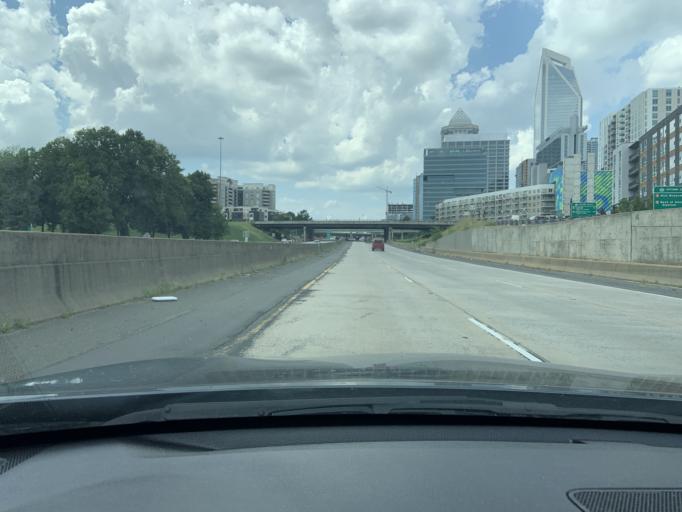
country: US
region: North Carolina
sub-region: Mecklenburg County
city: Charlotte
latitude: 35.2179
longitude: -80.8447
